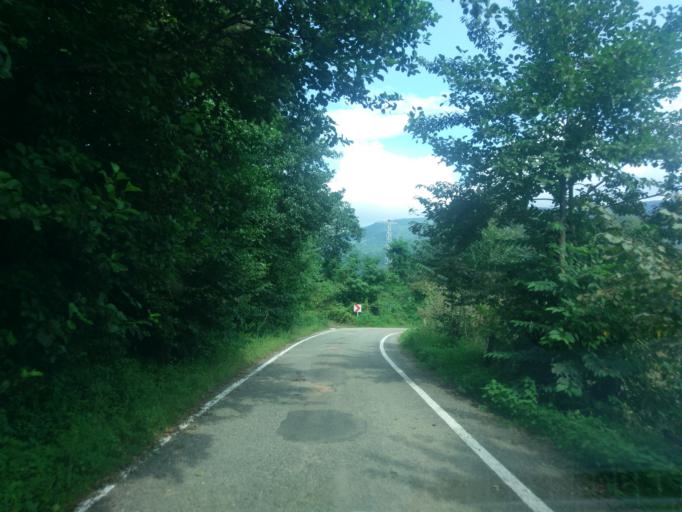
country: TR
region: Ordu
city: Camas
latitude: 40.9274
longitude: 37.6169
